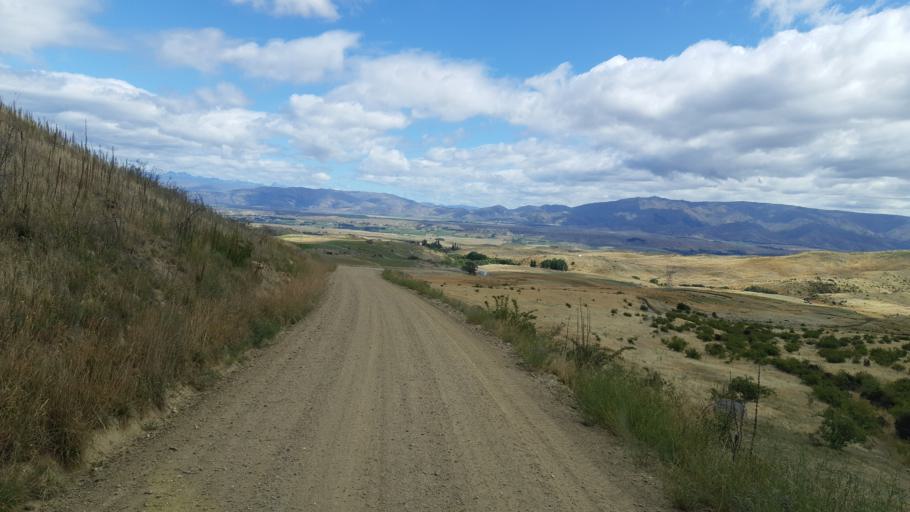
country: NZ
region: Otago
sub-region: Queenstown-Lakes District
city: Wanaka
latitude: -45.2174
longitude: 169.5683
